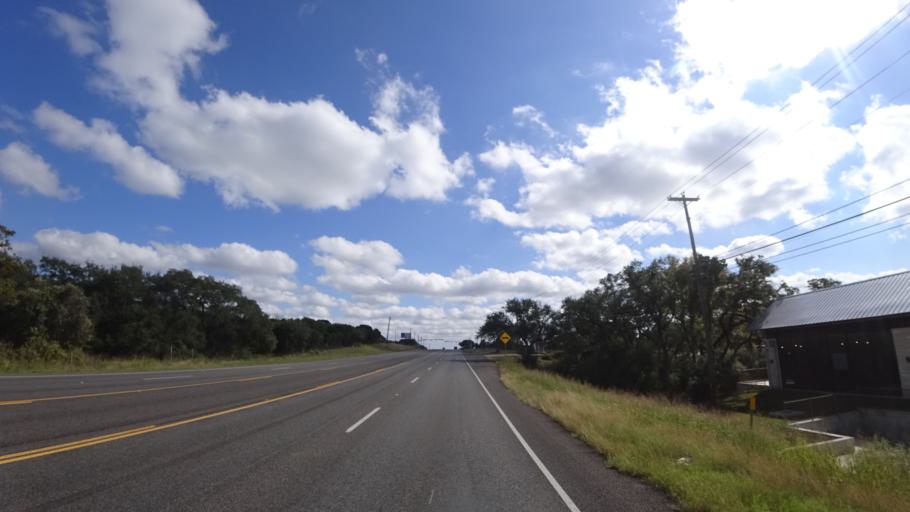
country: US
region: Texas
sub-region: Travis County
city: Barton Creek
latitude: 30.2509
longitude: -97.8966
